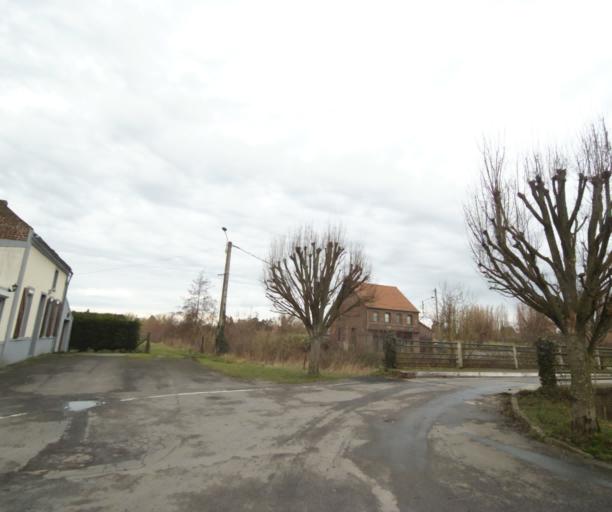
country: FR
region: Nord-Pas-de-Calais
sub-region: Departement du Nord
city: Hergnies
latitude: 50.4681
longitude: 3.5289
